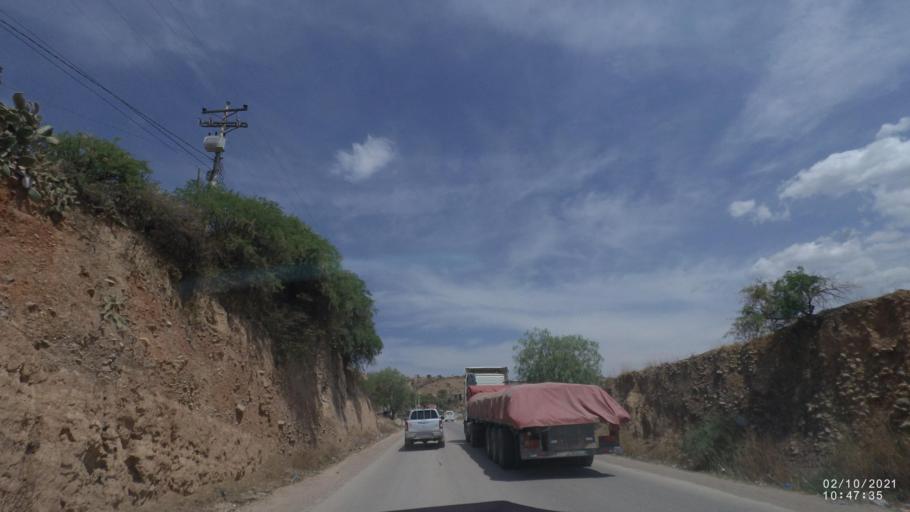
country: BO
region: Cochabamba
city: Sipe Sipe
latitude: -17.5826
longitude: -66.3306
